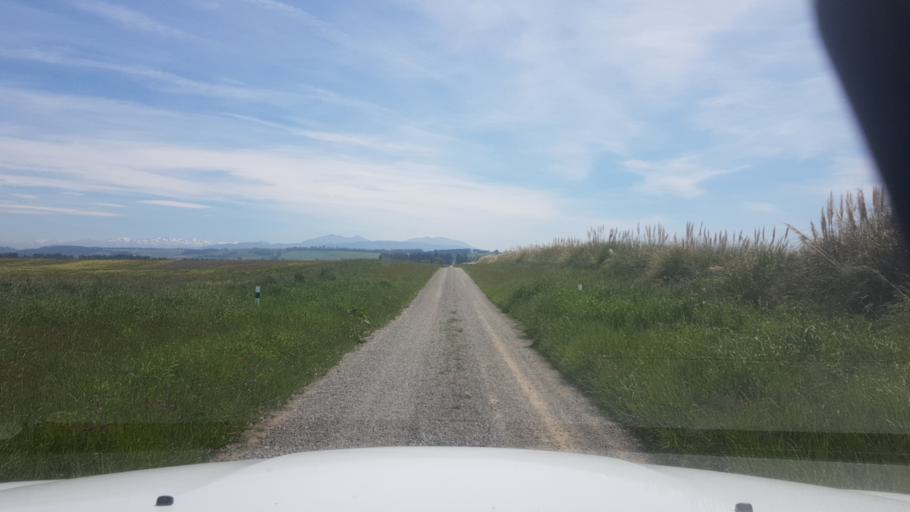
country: NZ
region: Canterbury
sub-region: Timaru District
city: Pleasant Point
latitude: -44.2347
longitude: 171.1680
